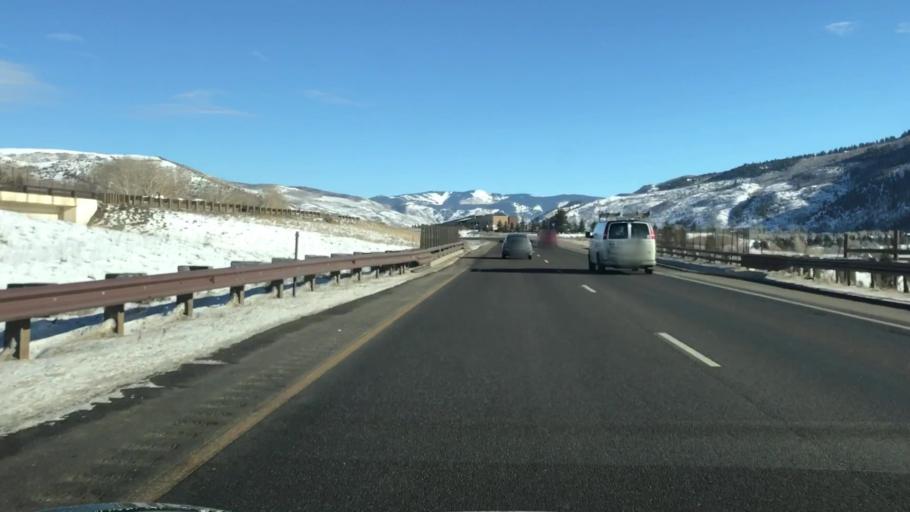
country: US
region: Colorado
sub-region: Eagle County
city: Edwards
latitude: 39.6433
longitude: -106.5746
